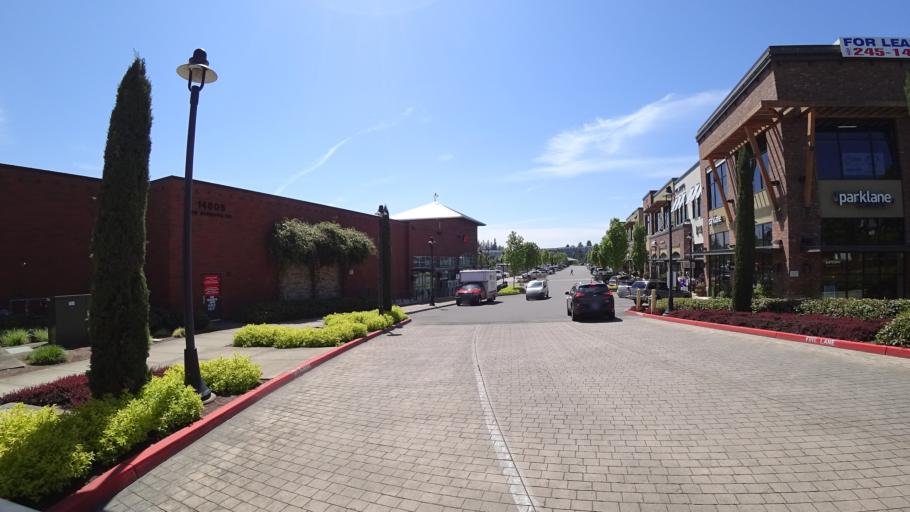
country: US
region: Oregon
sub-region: Washington County
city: King City
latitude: 45.4311
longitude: -122.8294
